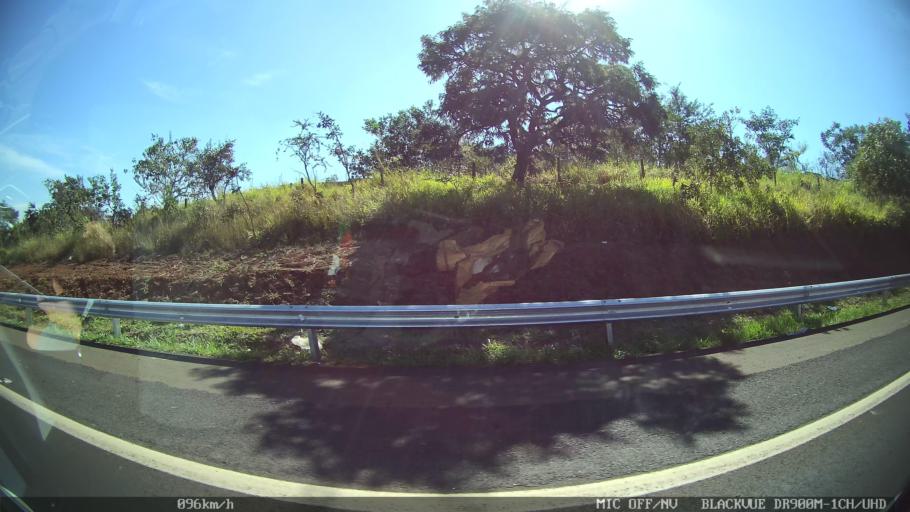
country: BR
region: Sao Paulo
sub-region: Franca
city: Franca
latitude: -20.5552
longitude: -47.4323
